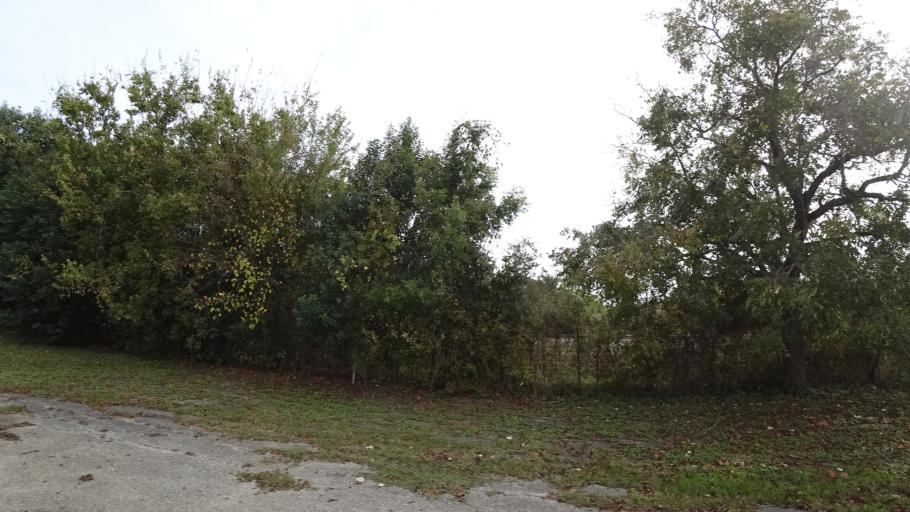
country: US
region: Texas
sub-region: Williamson County
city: Round Rock
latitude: 30.5123
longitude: -97.6607
